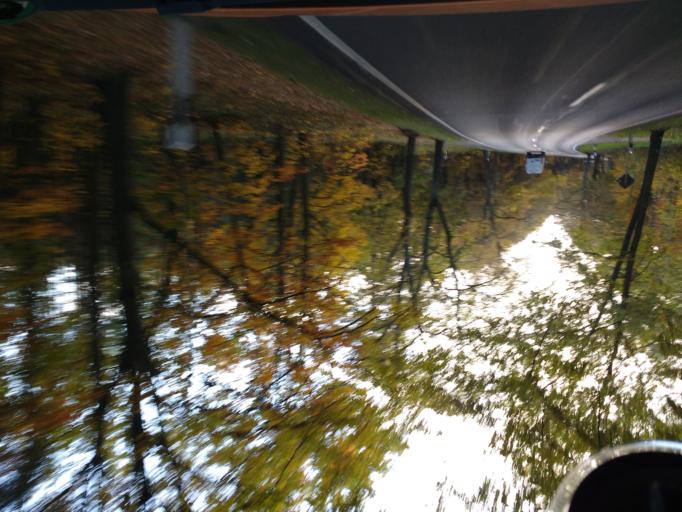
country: DE
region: Brandenburg
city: Grunheide
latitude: 52.4258
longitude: 13.7946
